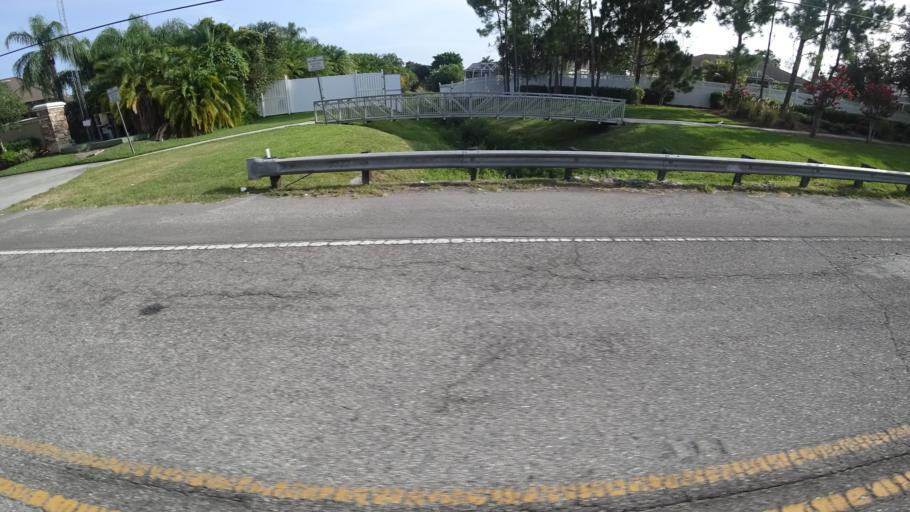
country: US
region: Florida
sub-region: Manatee County
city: Ellenton
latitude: 27.5468
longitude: -82.5029
